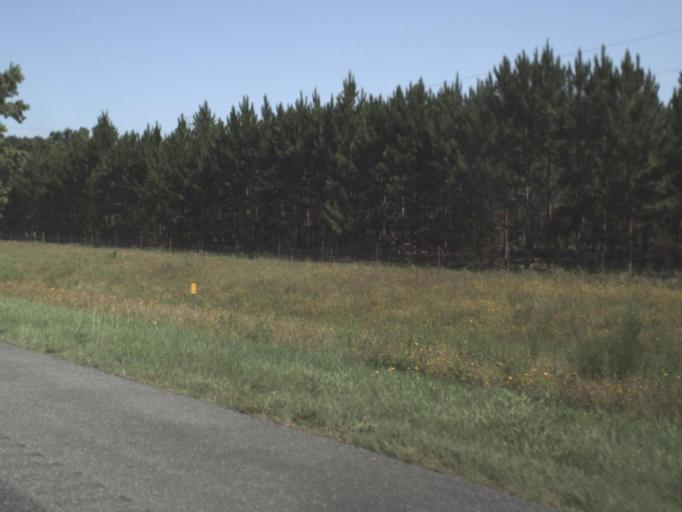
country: US
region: Florida
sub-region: Suwannee County
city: Live Oak
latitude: 30.3146
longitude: -82.9385
